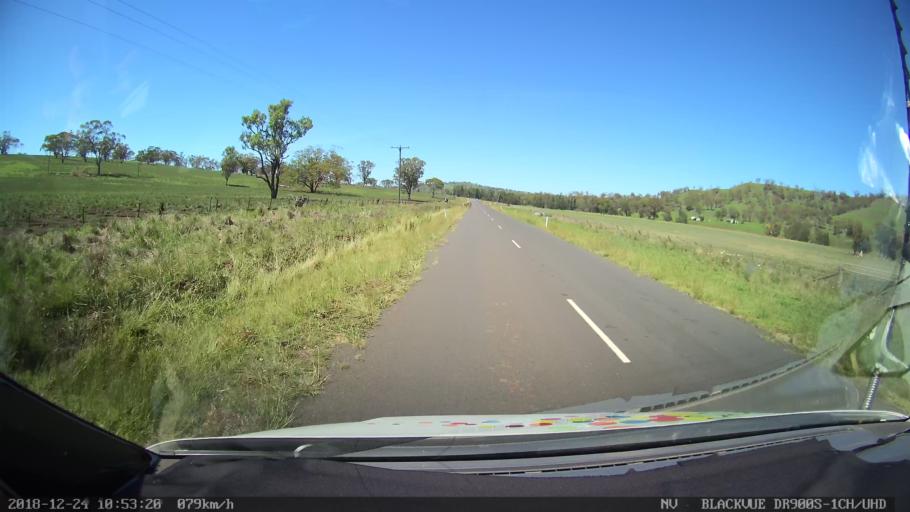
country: AU
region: New South Wales
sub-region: Upper Hunter Shire
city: Merriwa
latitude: -31.9904
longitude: 150.4217
